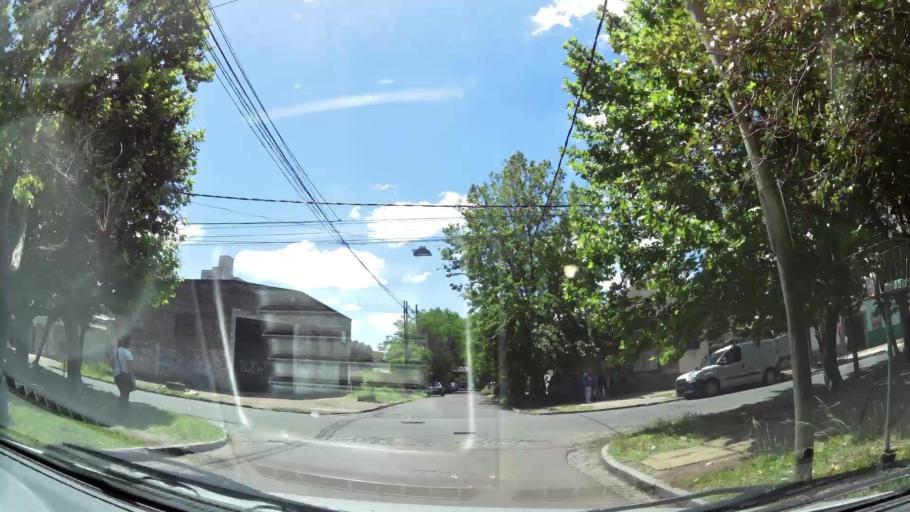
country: AR
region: Buenos Aires
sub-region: Partido de Lomas de Zamora
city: Lomas de Zamora
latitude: -34.7337
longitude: -58.4000
